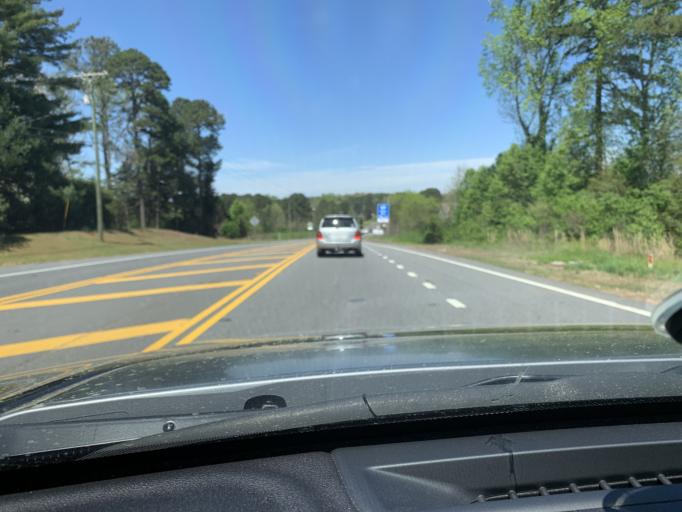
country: US
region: Georgia
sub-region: Fulton County
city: Milton
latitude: 34.1606
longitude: -84.2364
